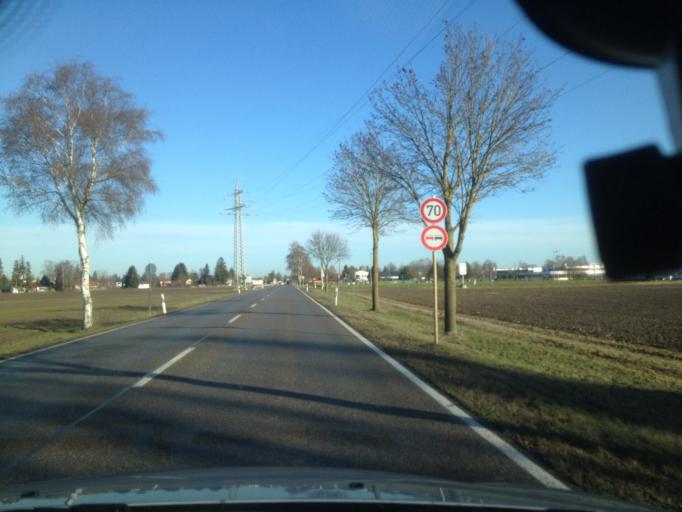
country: DE
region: Bavaria
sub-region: Swabia
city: Gundelfingen
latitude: 48.5376
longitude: 10.3634
